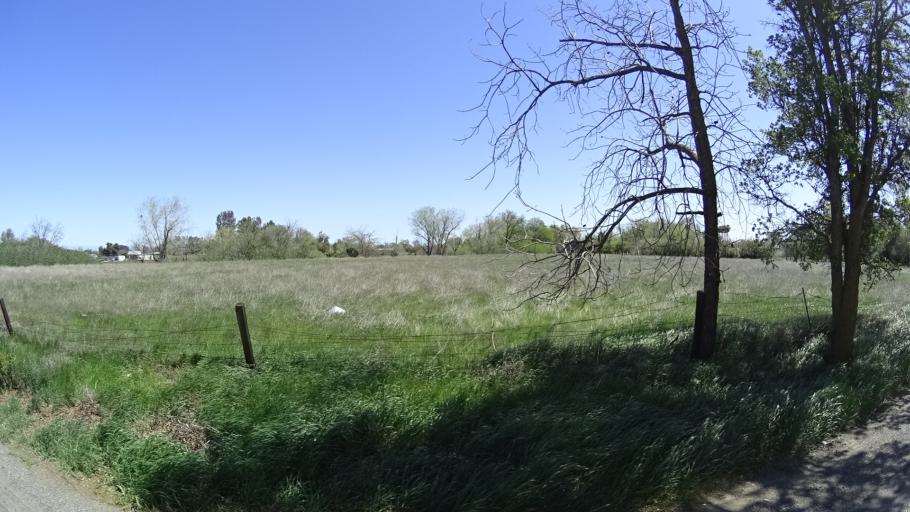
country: US
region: California
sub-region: Glenn County
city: Orland
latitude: 39.7740
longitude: -122.2477
